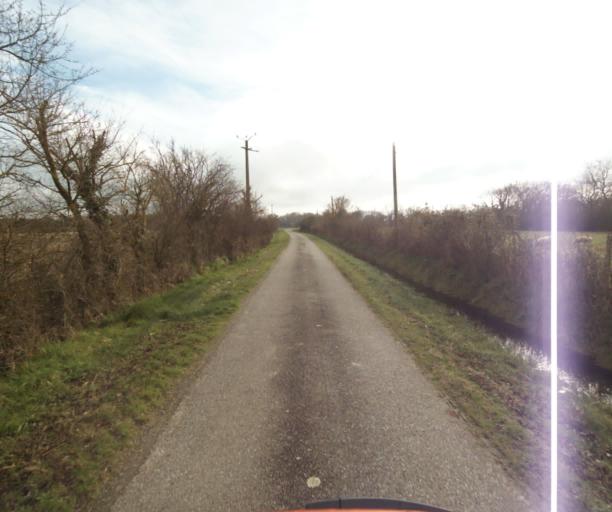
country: FR
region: Midi-Pyrenees
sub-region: Departement de l'Ariege
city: Mazeres
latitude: 43.2118
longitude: 1.6800
